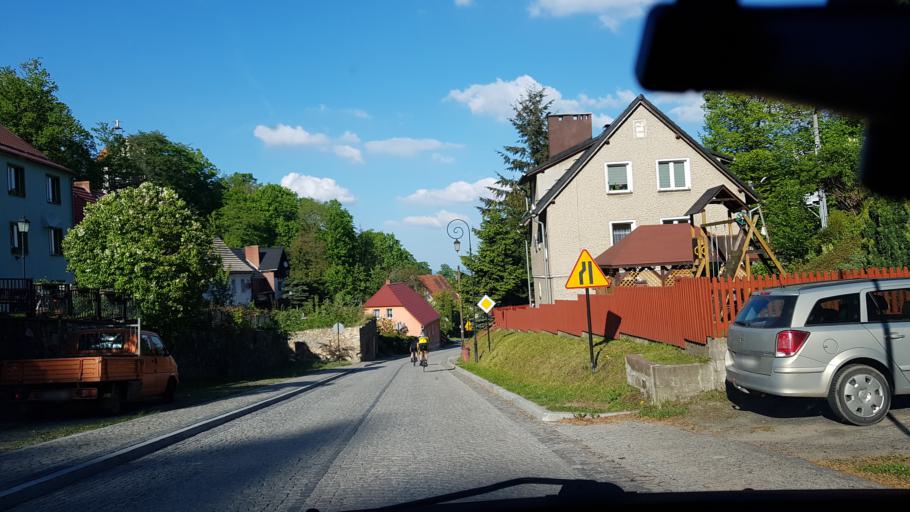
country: PL
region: Lower Silesian Voivodeship
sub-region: Powiat zabkowicki
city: Budzow
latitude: 50.5747
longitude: 16.6535
